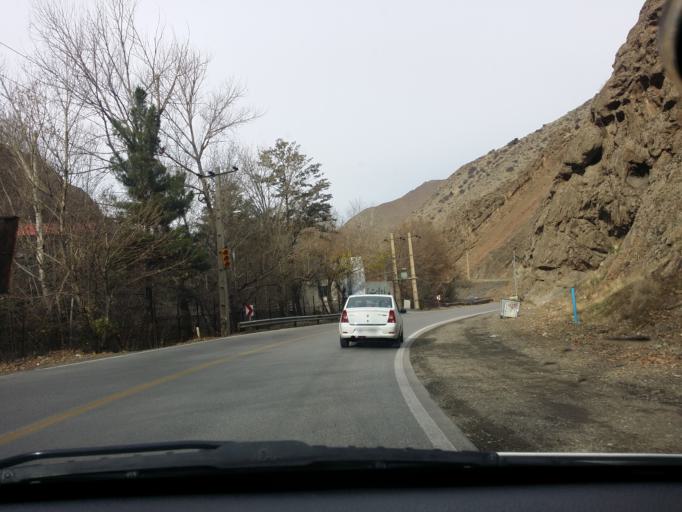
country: IR
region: Tehran
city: Tajrish
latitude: 36.0215
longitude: 51.2650
